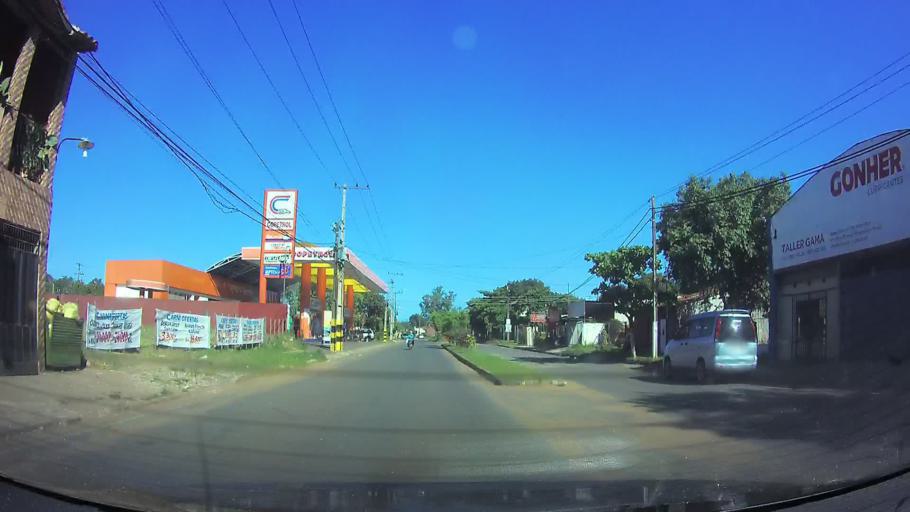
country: PY
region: Central
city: San Lorenzo
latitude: -25.2986
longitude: -57.5085
